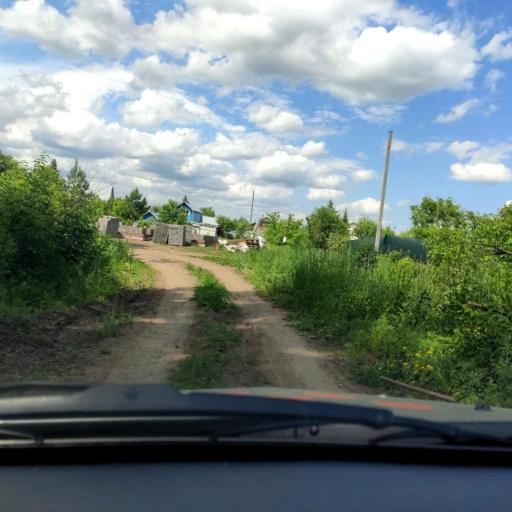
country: RU
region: Bashkortostan
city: Ufa
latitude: 54.7830
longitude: 56.1885
